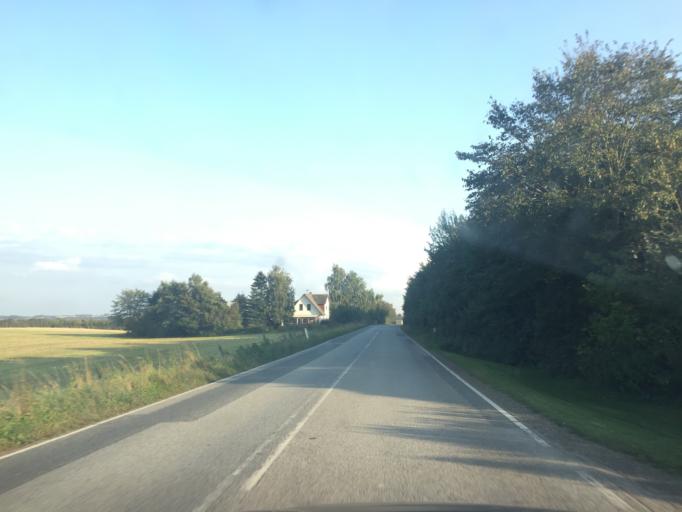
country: DK
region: Zealand
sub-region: Kalundborg Kommune
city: Svebolle
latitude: 55.6042
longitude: 11.2701
